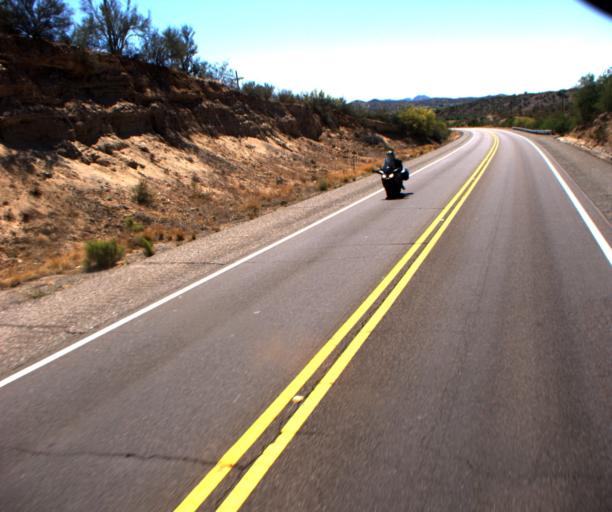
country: US
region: Arizona
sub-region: Maricopa County
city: Wickenburg
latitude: 33.9949
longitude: -112.7546
